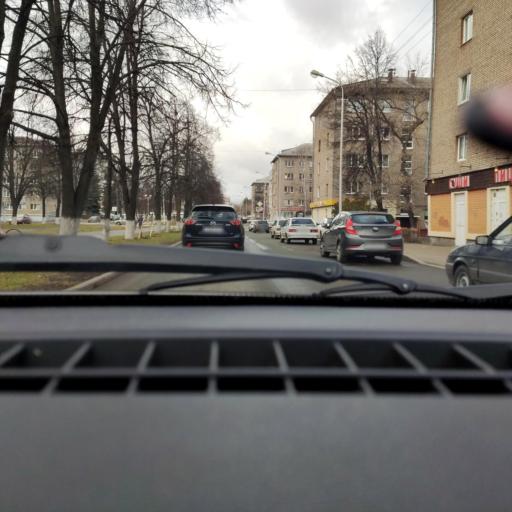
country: RU
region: Bashkortostan
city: Ufa
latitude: 54.7906
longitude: 56.0327
